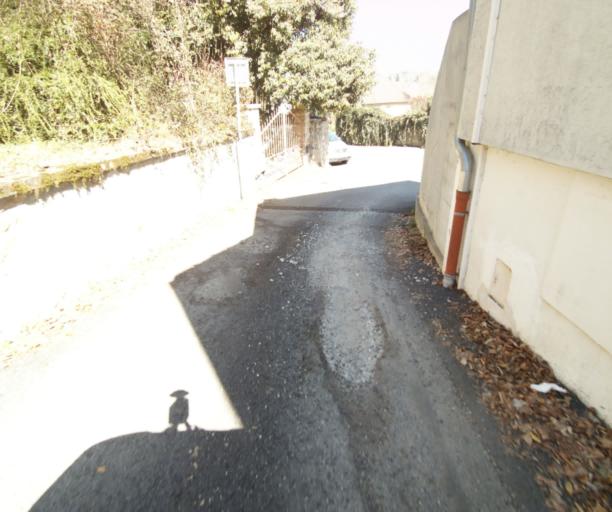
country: FR
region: Limousin
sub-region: Departement de la Correze
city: Seilhac
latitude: 45.3678
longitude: 1.7125
